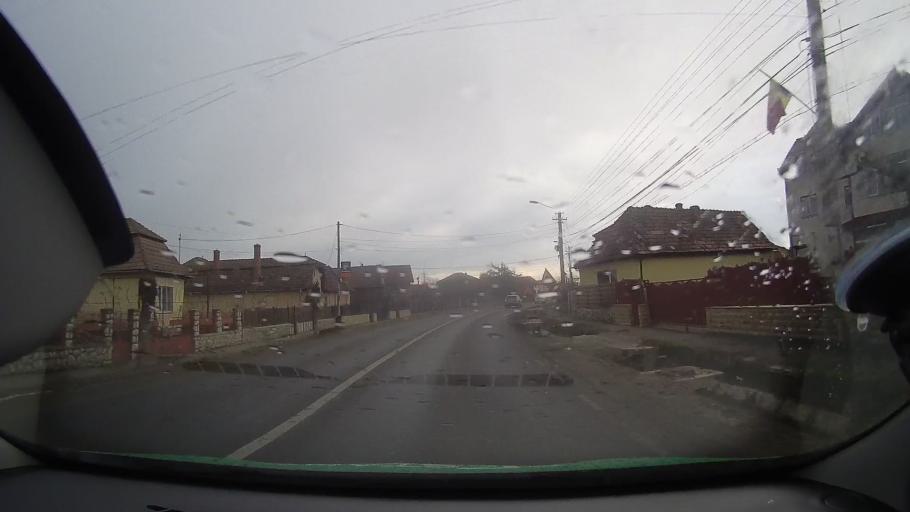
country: RO
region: Cluj
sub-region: Municipiul Campia Turzii
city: Campia Turzii
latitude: 46.5585
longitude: 23.8433
